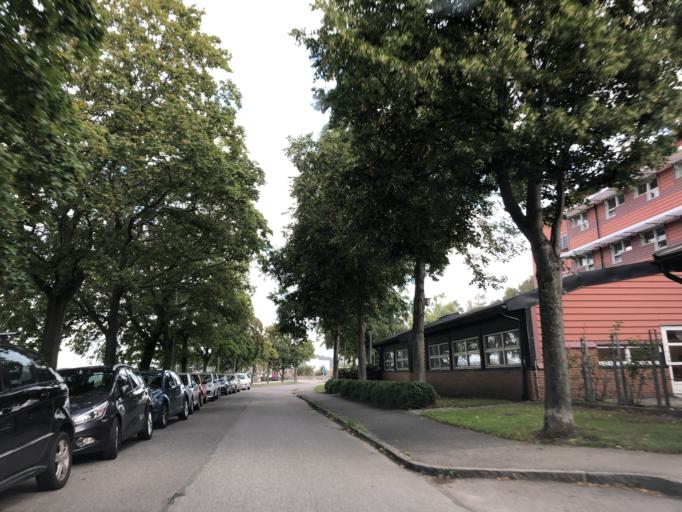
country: SE
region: Vaestra Goetaland
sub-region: Goteborg
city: Goeteborg
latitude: 57.7216
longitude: 12.0115
